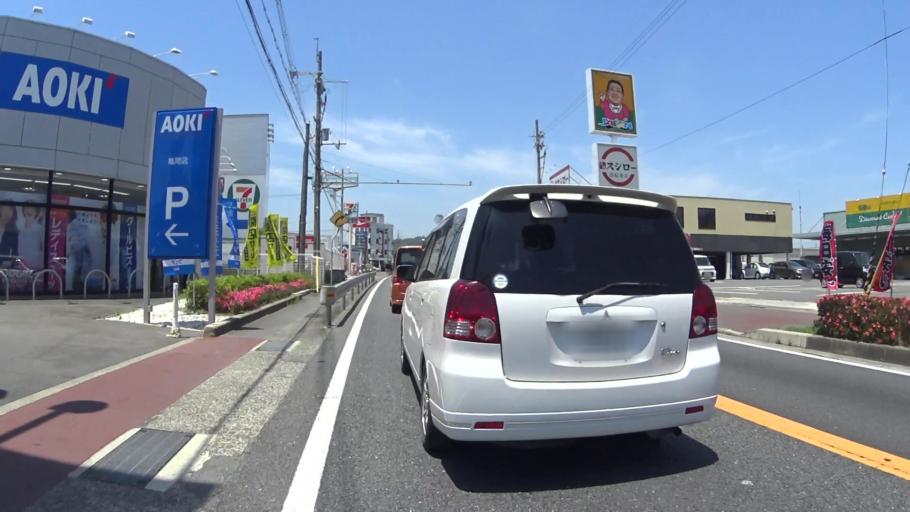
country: JP
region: Kyoto
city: Kameoka
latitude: 35.1242
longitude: 135.4504
